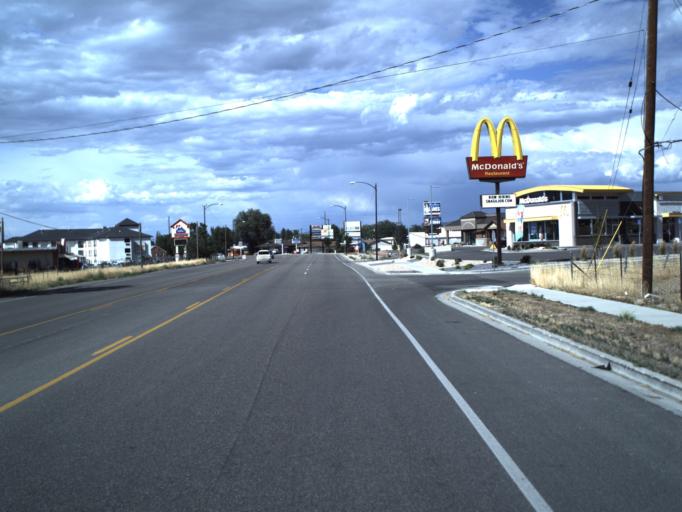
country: US
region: Utah
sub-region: Sanpete County
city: Ephraim
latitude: 39.3493
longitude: -111.5885
